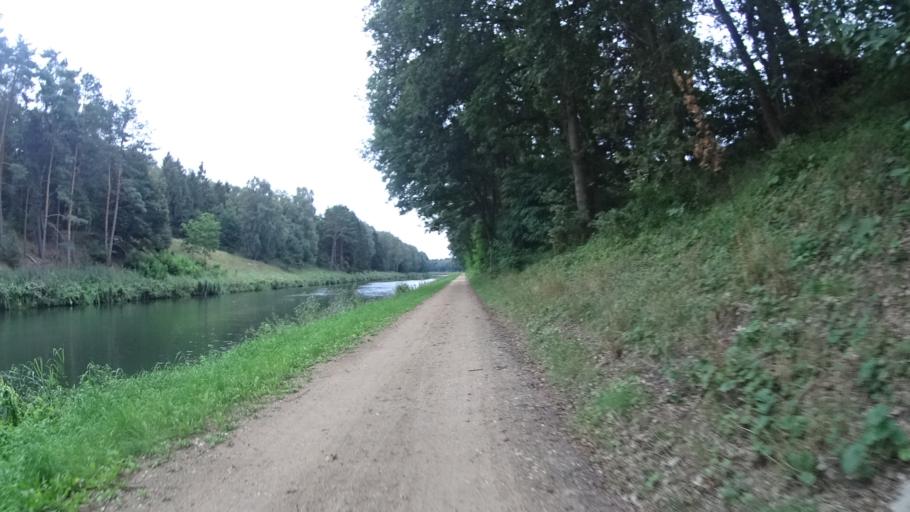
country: DE
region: Schleswig-Holstein
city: Grambek
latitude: 53.5939
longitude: 10.6658
